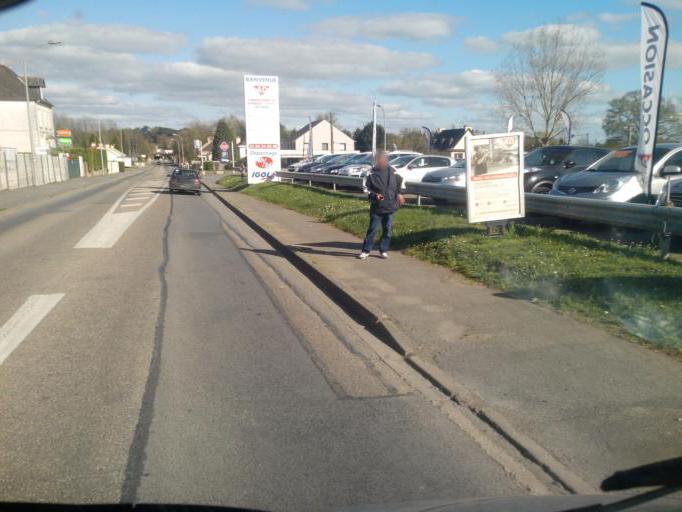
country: FR
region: Brittany
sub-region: Departement d'Ille-et-Vilaine
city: Guipry
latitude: 47.8223
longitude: -1.8335
